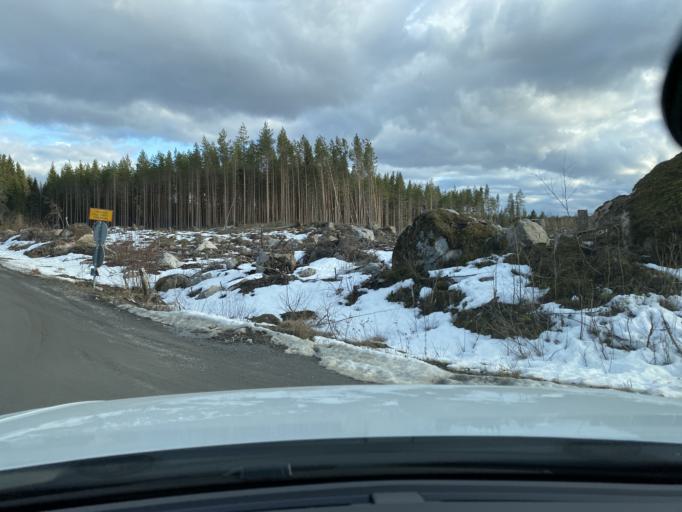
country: FI
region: Pirkanmaa
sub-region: Lounais-Pirkanmaa
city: Mouhijaervi
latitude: 61.4336
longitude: 22.9657
